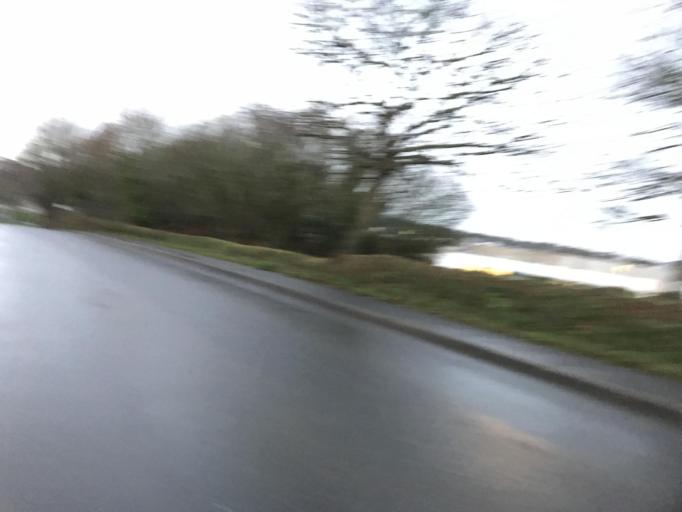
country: FR
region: Brittany
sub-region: Departement du Finistere
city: Plougastel-Daoulas
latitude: 48.3698
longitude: -4.3622
